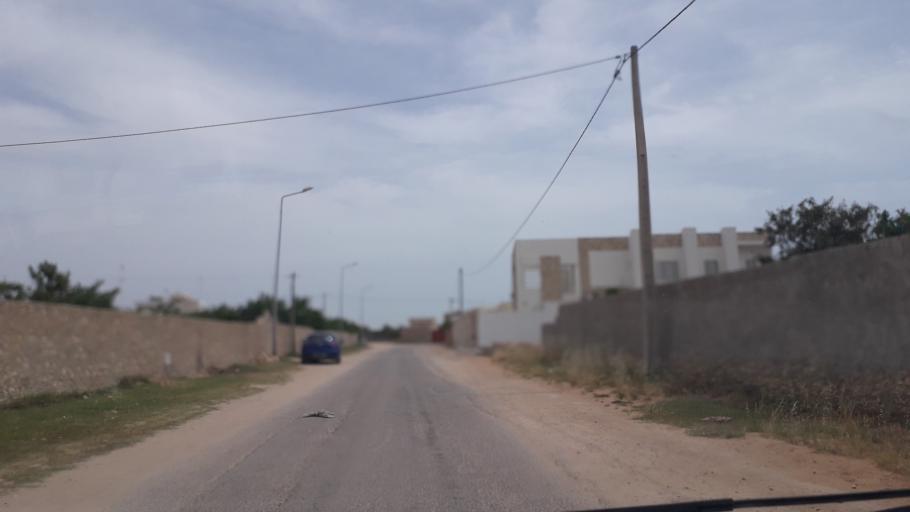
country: TN
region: Safaqis
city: Al Qarmadah
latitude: 34.8093
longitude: 10.7702
